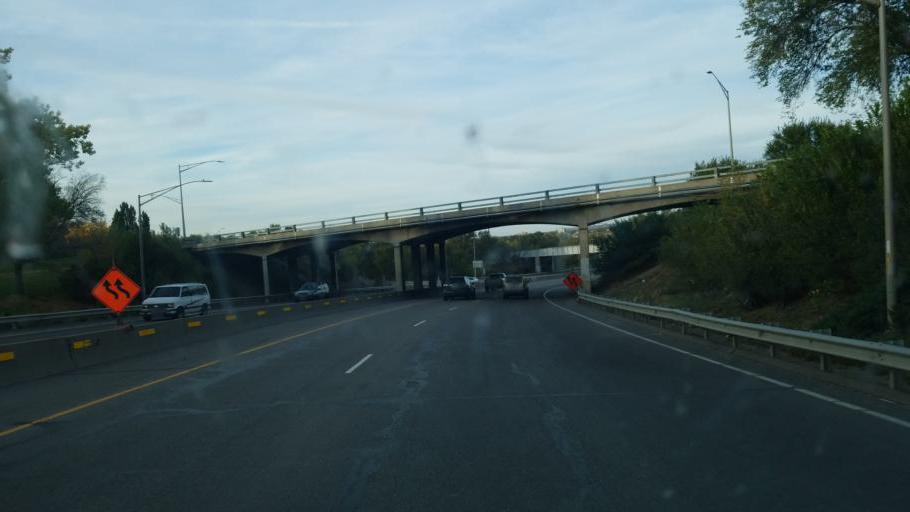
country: US
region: Colorado
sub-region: Pueblo County
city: Pueblo
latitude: 38.2522
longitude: -104.6095
